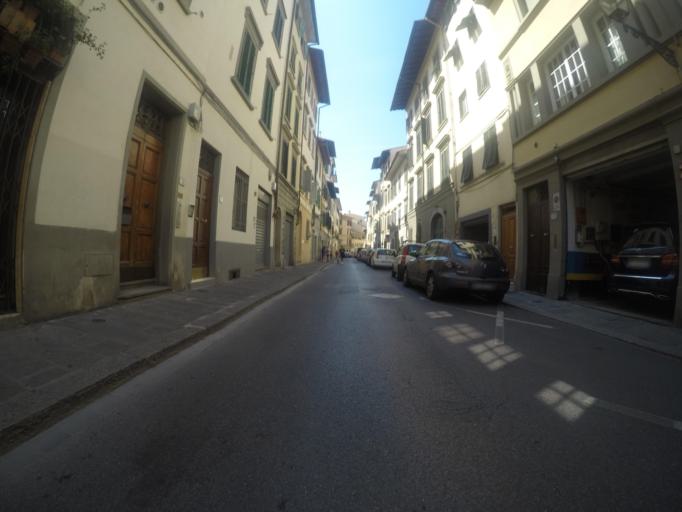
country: IT
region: Tuscany
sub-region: Province of Florence
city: Florence
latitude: 43.7787
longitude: 11.2550
